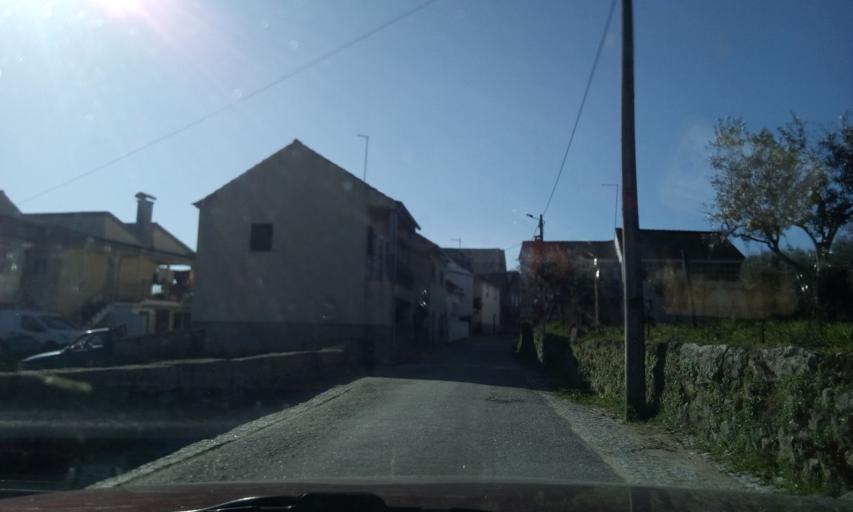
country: PT
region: Guarda
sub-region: Celorico da Beira
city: Celorico da Beira
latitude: 40.6766
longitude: -7.3970
